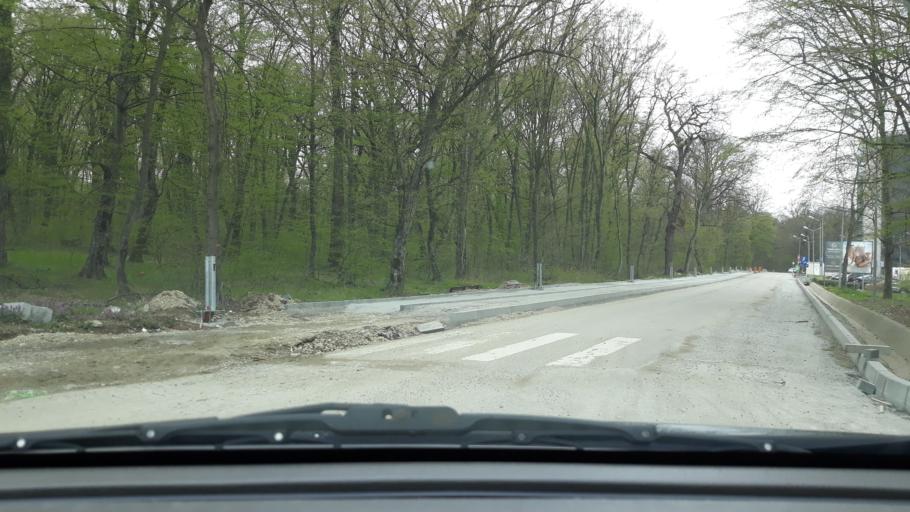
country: RO
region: Bihor
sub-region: Comuna Sanmartin
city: Sanmartin
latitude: 46.9878
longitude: 21.9762
